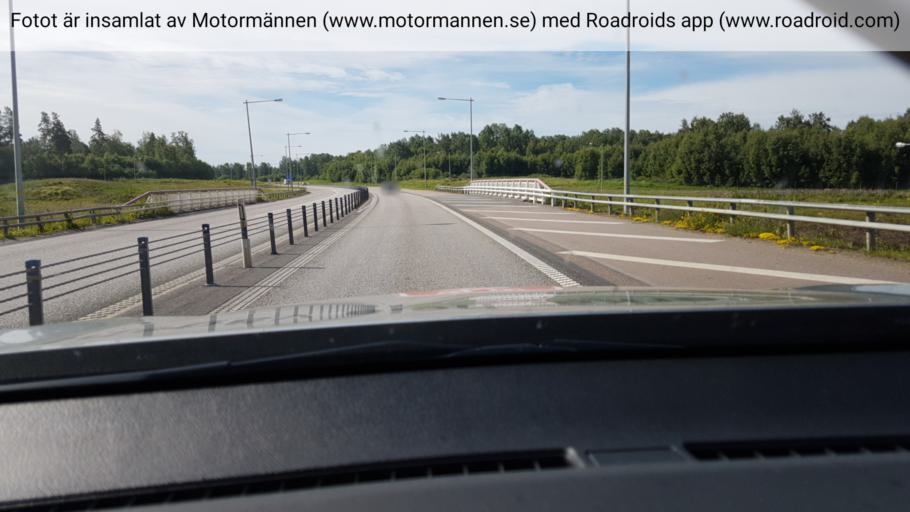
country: SE
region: Vaestra Goetaland
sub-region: Skovde Kommun
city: Skoevde
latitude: 58.3686
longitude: 13.8550
